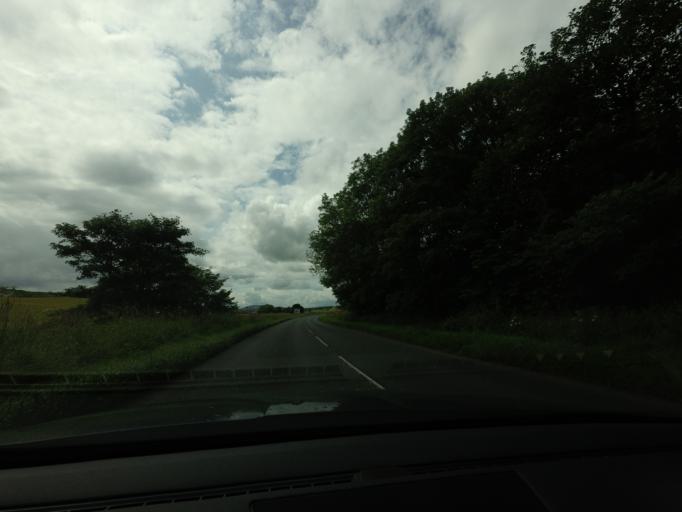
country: GB
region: Scotland
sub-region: Aberdeenshire
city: Whitehills
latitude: 57.6627
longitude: -2.5803
